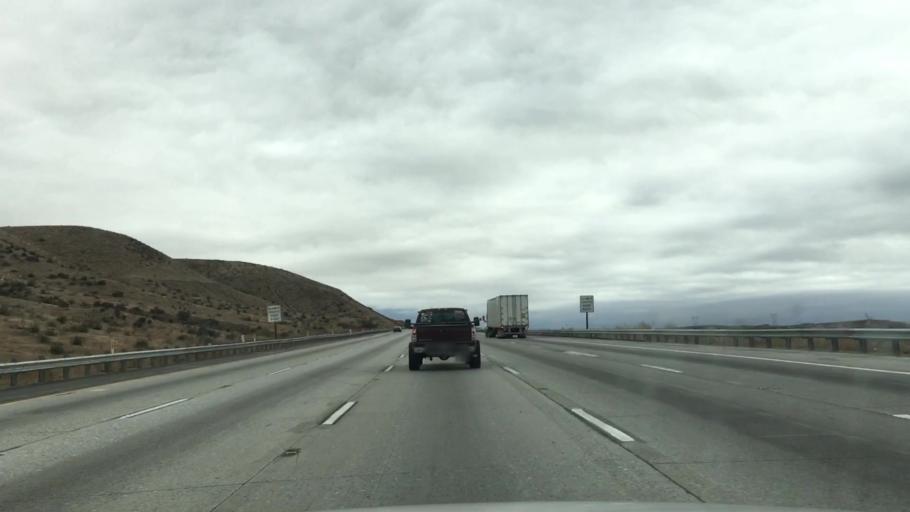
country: US
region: California
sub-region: San Bernardino County
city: Oak Hills
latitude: 34.3416
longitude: -117.4560
